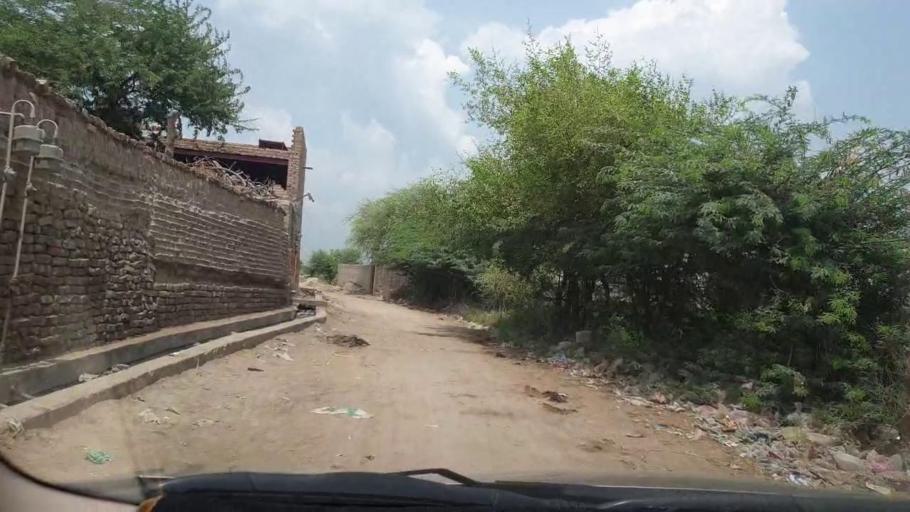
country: PK
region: Sindh
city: Larkana
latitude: 27.5675
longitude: 68.1262
